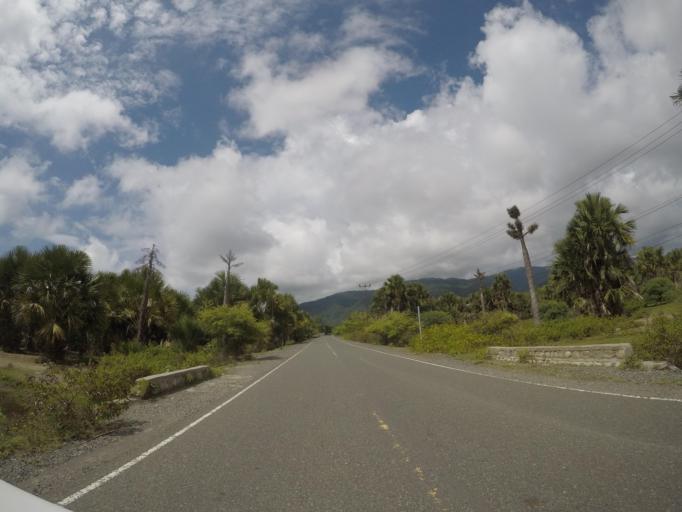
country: TL
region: Liquica
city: Maubara
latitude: -8.7211
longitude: 125.1099
